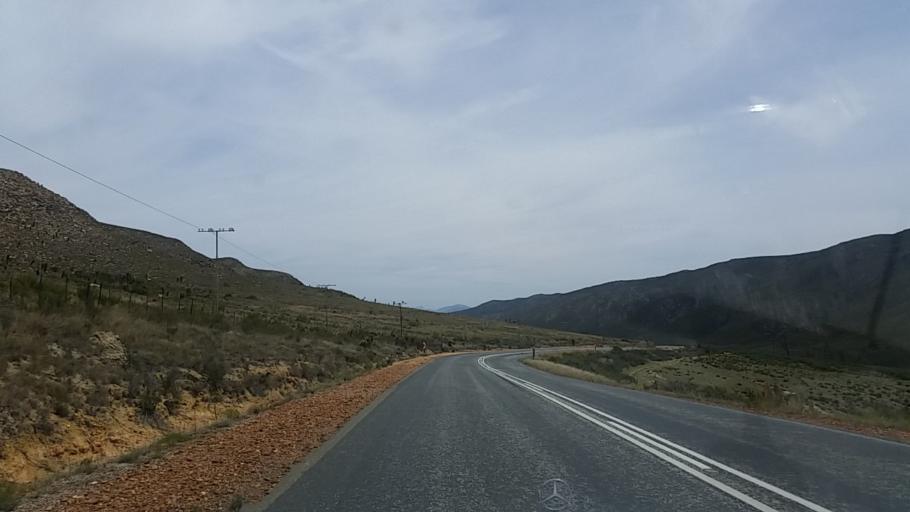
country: ZA
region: Western Cape
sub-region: Eden District Municipality
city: Knysna
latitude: -33.7426
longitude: 23.0070
